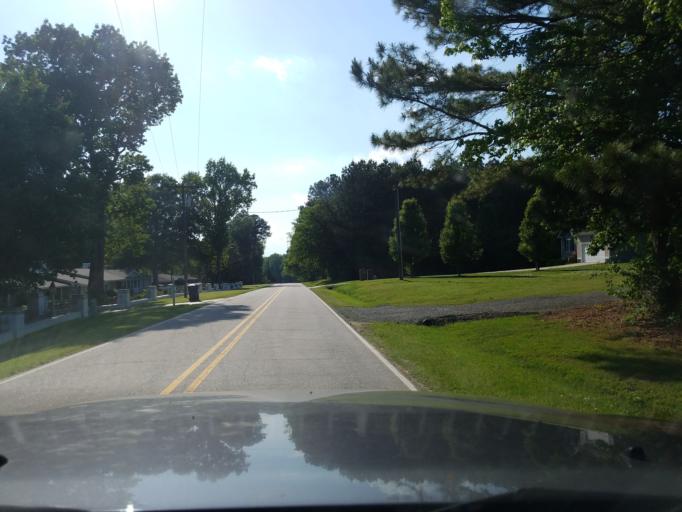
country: US
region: North Carolina
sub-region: Vance County
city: Henderson
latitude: 36.4076
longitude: -78.3752
